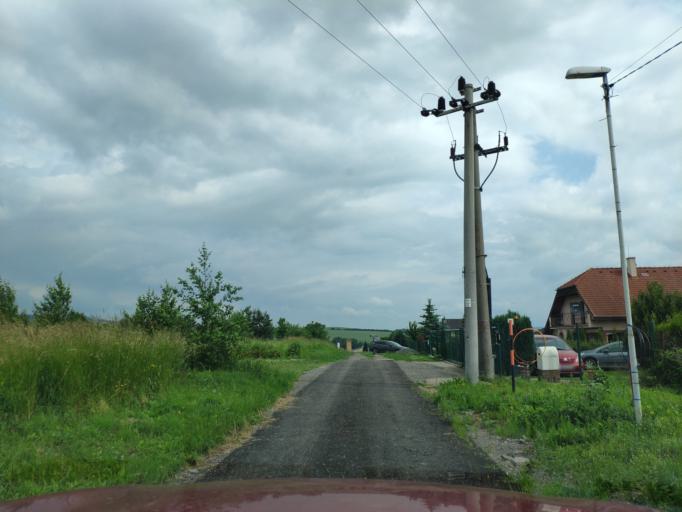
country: SK
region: Kosicky
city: Kosice
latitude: 48.8030
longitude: 21.2987
